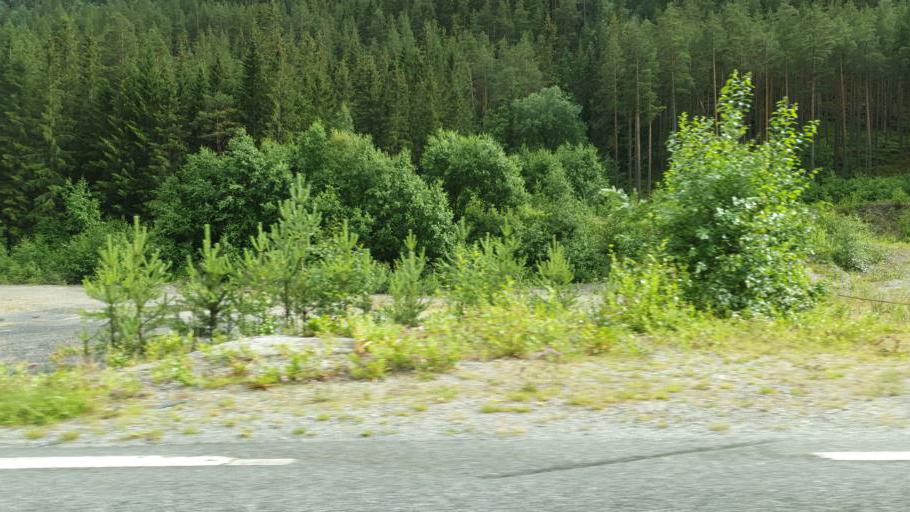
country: NO
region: Oppland
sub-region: Dovre
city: Dovre
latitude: 61.8497
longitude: 9.3068
